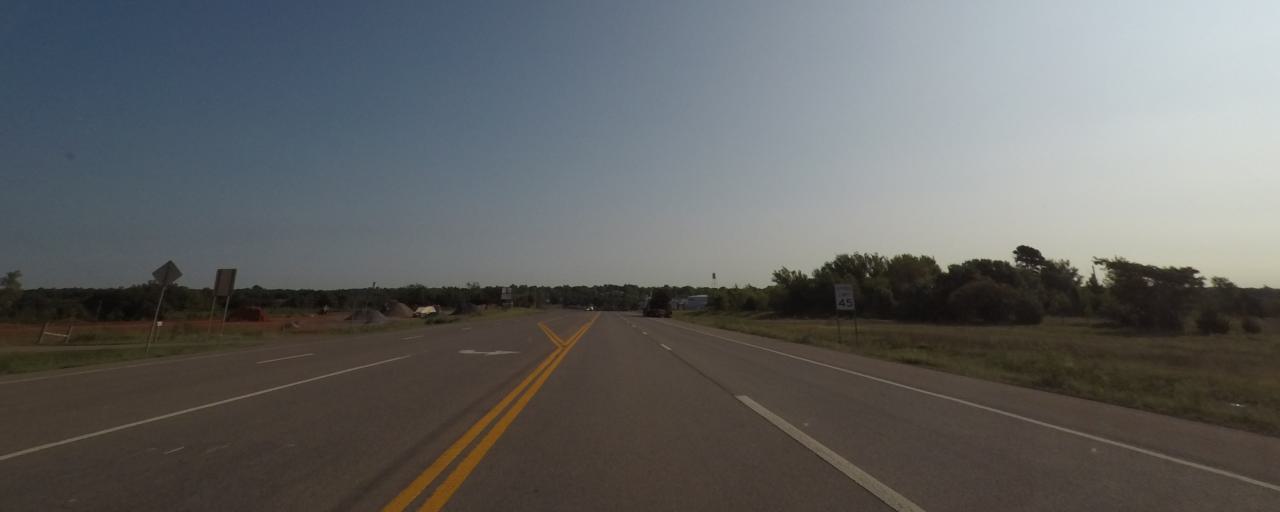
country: US
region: Oklahoma
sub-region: McClain County
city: Blanchard
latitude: 35.1284
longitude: -97.6691
